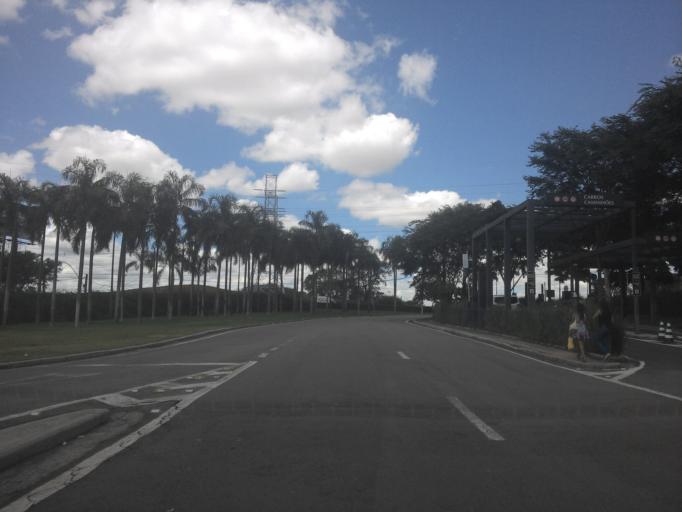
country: BR
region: Sao Paulo
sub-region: Campinas
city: Campinas
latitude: -22.8930
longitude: -47.0250
